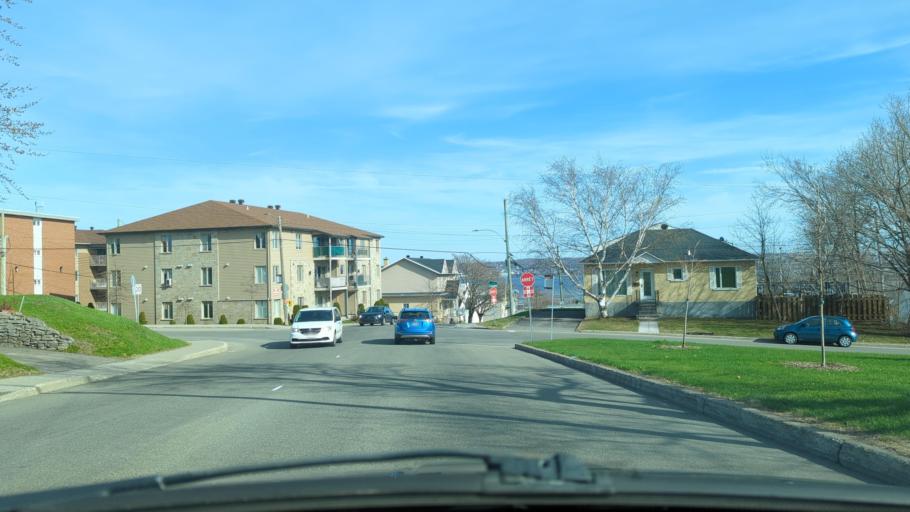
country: CA
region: Quebec
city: Quebec
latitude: 46.8570
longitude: -71.2080
